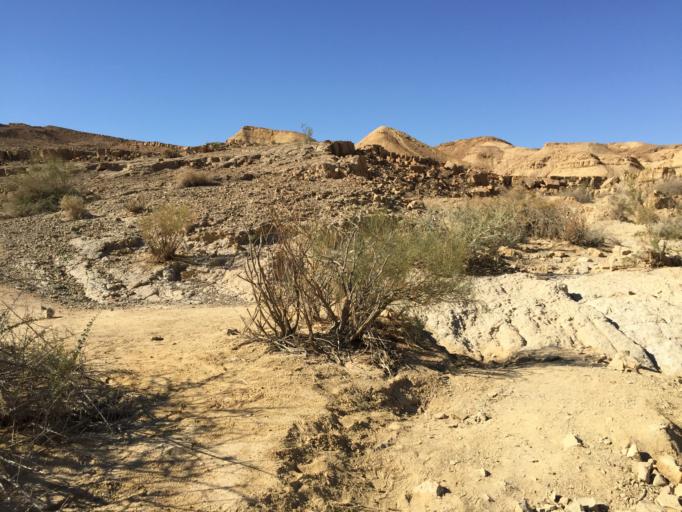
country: IL
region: Southern District
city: Mitzpe Ramon
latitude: 30.6031
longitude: 34.9491
